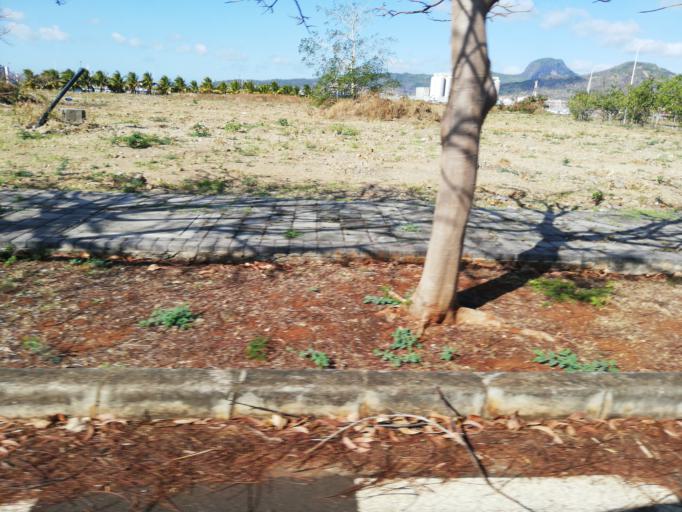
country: MU
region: Port Louis
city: Port Louis
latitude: -20.1577
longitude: 57.4921
